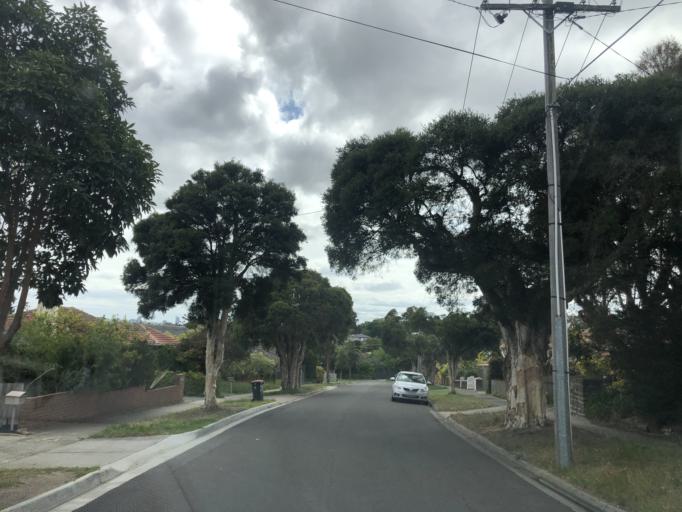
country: AU
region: Victoria
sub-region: Monash
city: Chadstone
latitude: -37.8788
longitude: 145.1020
